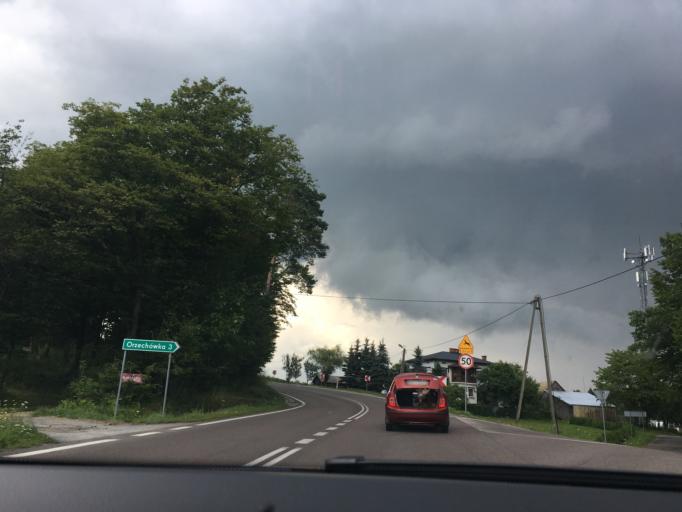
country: PL
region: Subcarpathian Voivodeship
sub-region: Powiat brzozowski
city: Jablonica Polska
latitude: 49.7243
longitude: 21.9084
